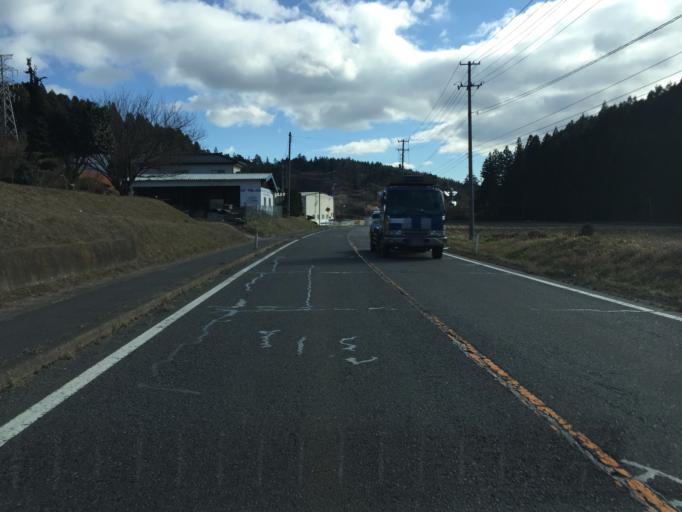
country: JP
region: Fukushima
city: Ishikawa
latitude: 37.2281
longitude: 140.5821
